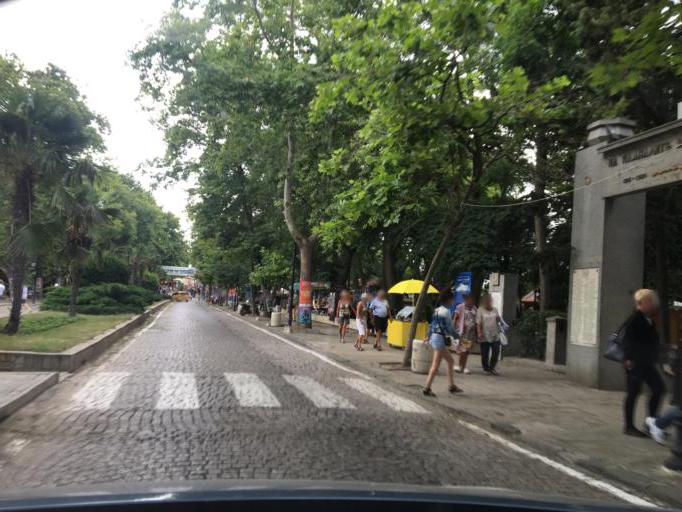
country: BG
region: Burgas
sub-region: Obshtina Sozopol
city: Sozopol
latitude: 42.4202
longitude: 27.6935
